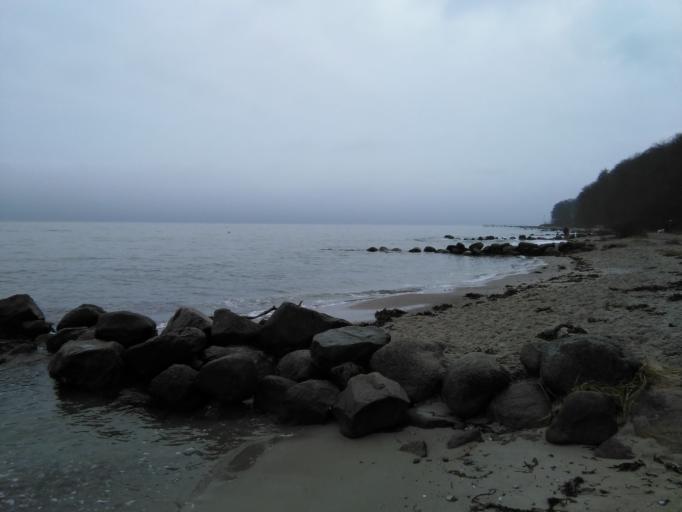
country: DK
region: Central Jutland
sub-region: Arhus Kommune
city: Arhus
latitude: 56.1241
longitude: 10.2192
